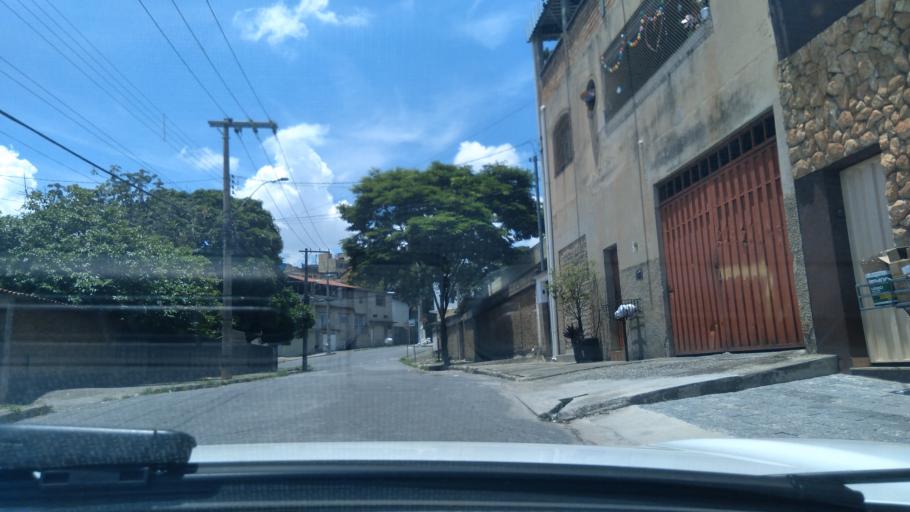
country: BR
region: Minas Gerais
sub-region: Contagem
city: Contagem
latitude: -19.9278
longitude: -44.0113
